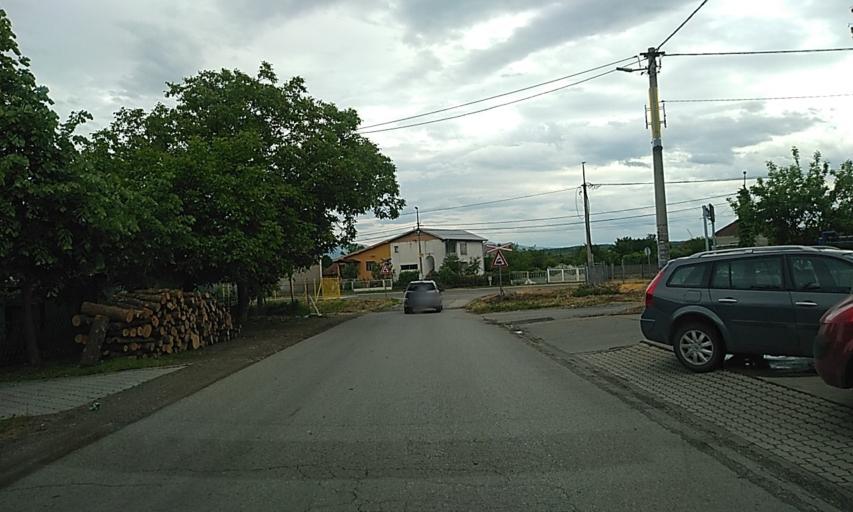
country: RS
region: Central Serbia
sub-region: Rasinski Okrug
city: Krusevac
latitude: 43.5872
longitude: 21.2873
